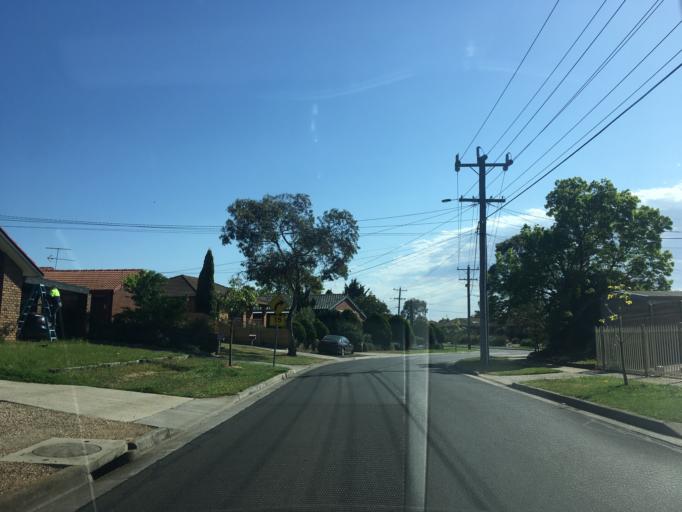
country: AU
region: Victoria
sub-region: Wyndham
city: Hoppers Crossing
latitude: -37.8733
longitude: 144.7034
